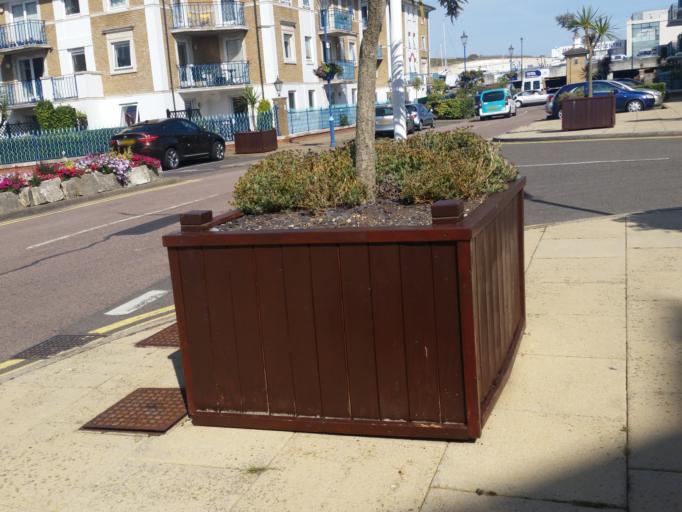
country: GB
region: England
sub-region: Brighton and Hove
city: Rottingdean
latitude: 50.8116
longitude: -0.0964
